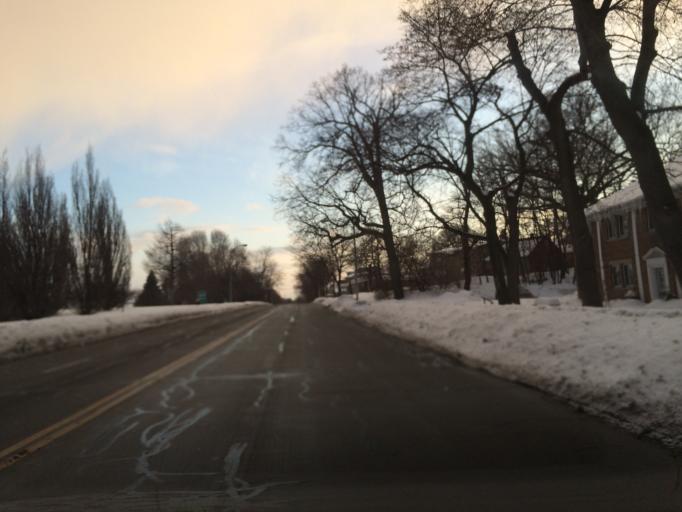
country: US
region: New York
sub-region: Monroe County
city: Rochester
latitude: 43.1297
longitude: -77.6112
